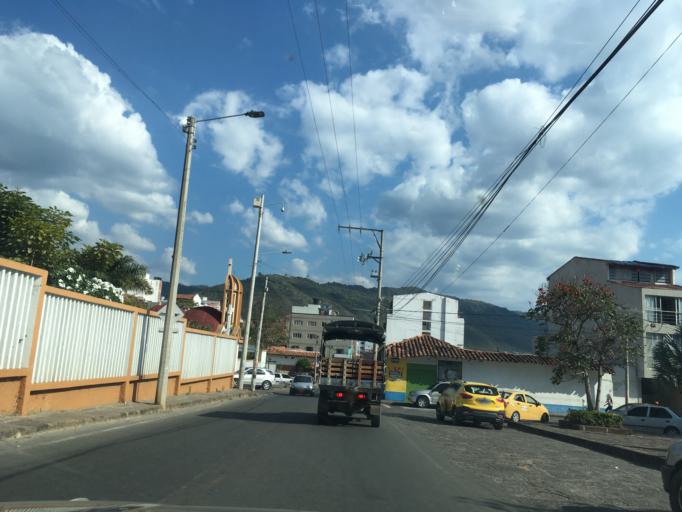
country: CO
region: Santander
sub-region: San Gil
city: San Gil
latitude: 6.5597
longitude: -73.1372
